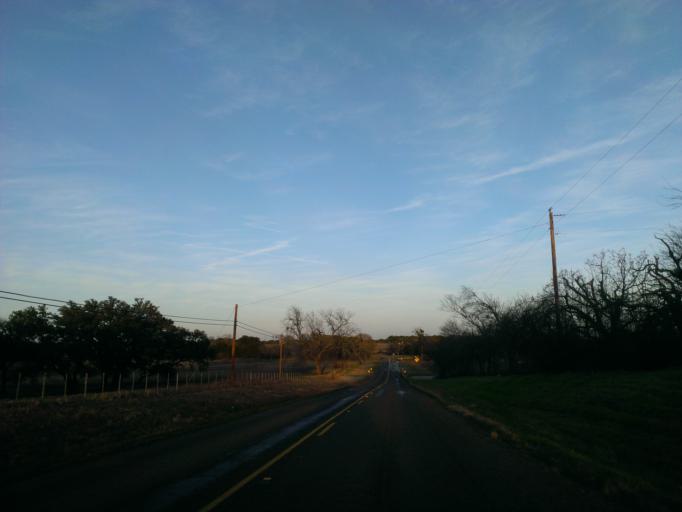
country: US
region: Texas
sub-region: Burnet County
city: Bertram
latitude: 30.7334
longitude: -98.0737
